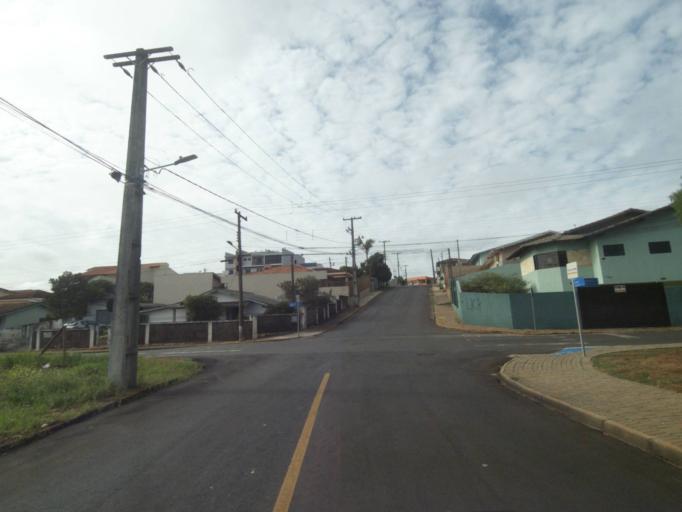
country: BR
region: Parana
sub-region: Telemaco Borba
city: Telemaco Borba
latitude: -24.3350
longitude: -50.6177
